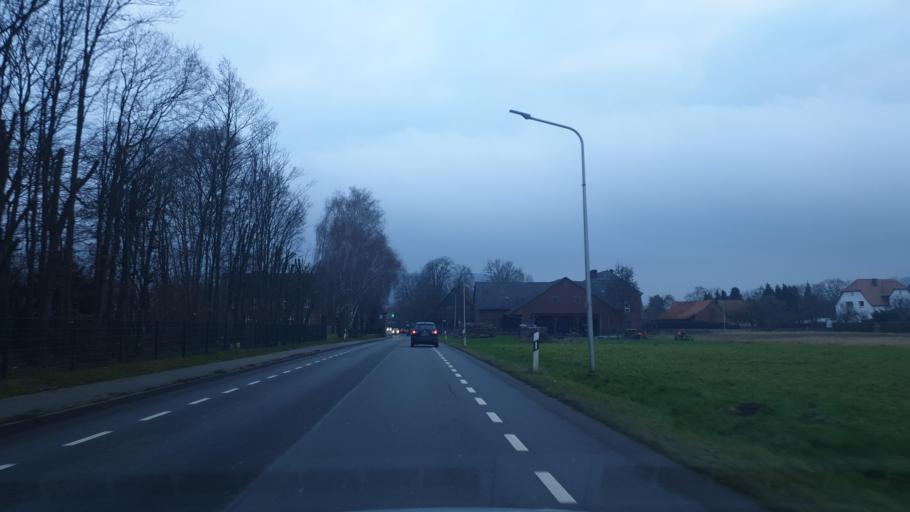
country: DE
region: North Rhine-Westphalia
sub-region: Regierungsbezirk Detmold
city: Minden
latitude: 52.2652
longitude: 8.9289
